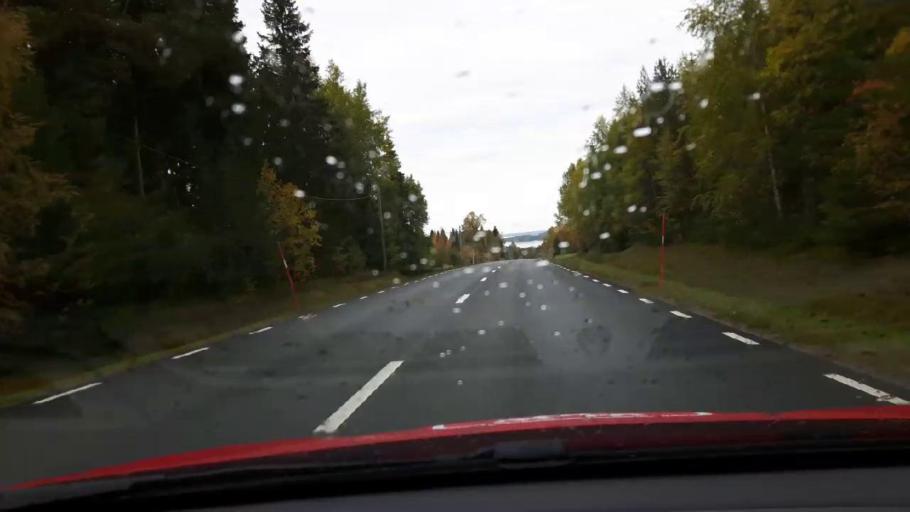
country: SE
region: Jaemtland
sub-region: Krokoms Kommun
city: Krokom
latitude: 63.1153
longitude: 14.2932
